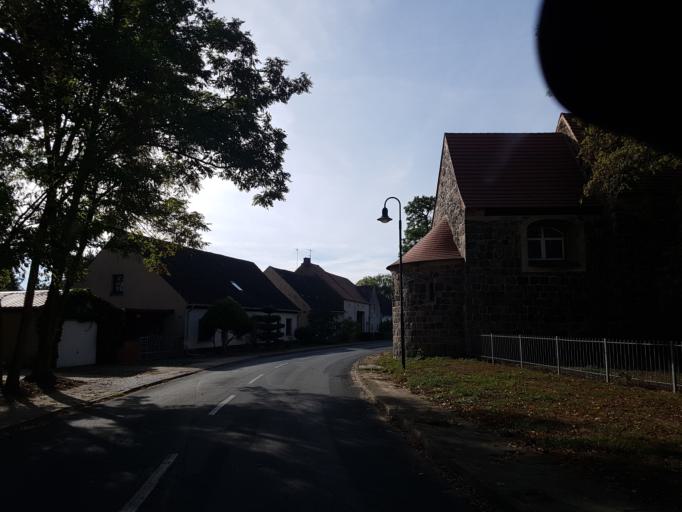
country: DE
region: Brandenburg
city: Ihlow
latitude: 51.9078
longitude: 13.2217
